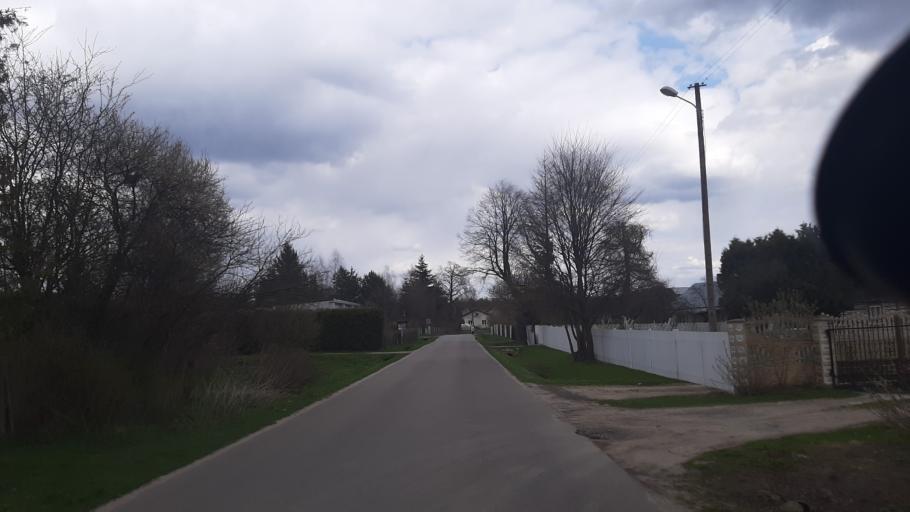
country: PL
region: Lublin Voivodeship
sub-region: Powiat lubelski
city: Niemce
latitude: 51.3838
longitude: 22.5583
